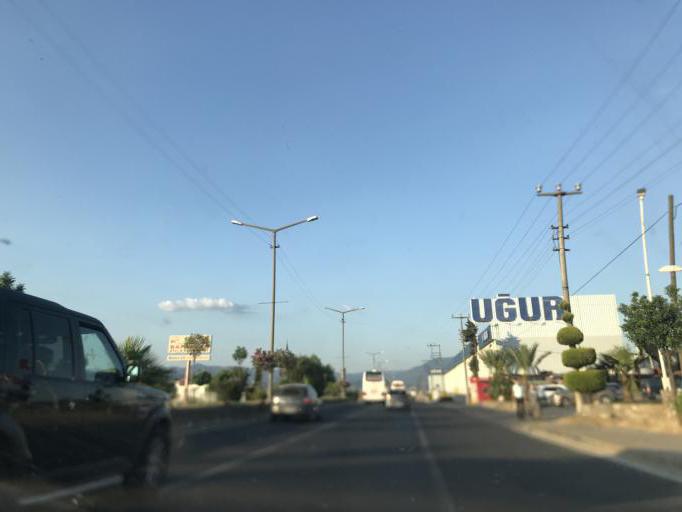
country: TR
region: Aydin
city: Nazilli
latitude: 37.9045
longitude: 28.3006
